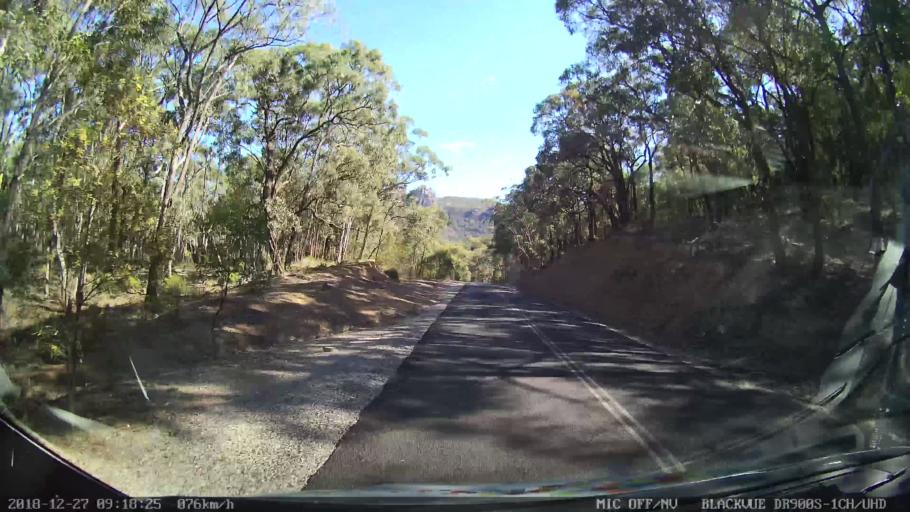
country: AU
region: New South Wales
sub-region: Lithgow
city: Portland
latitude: -33.1273
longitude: 150.0450
